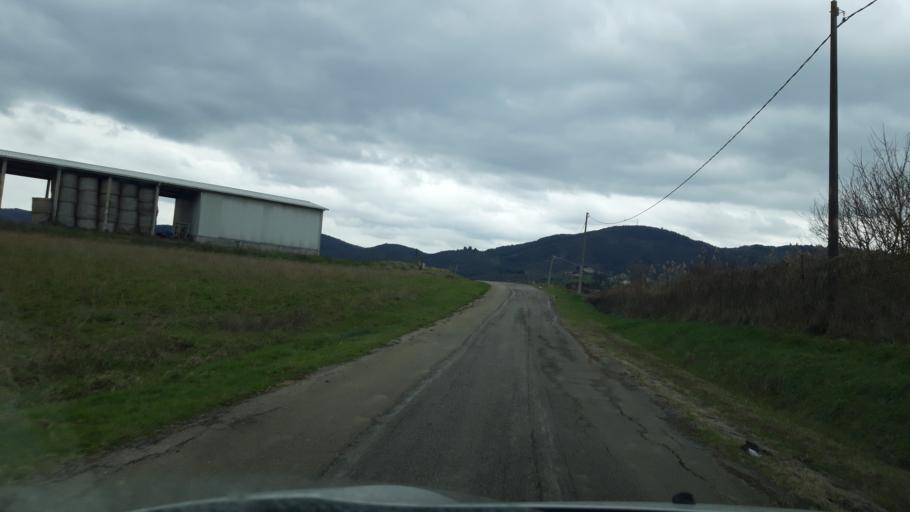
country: IT
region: Umbria
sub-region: Provincia di Perugia
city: Fontignano
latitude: 42.9932
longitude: 12.1805
